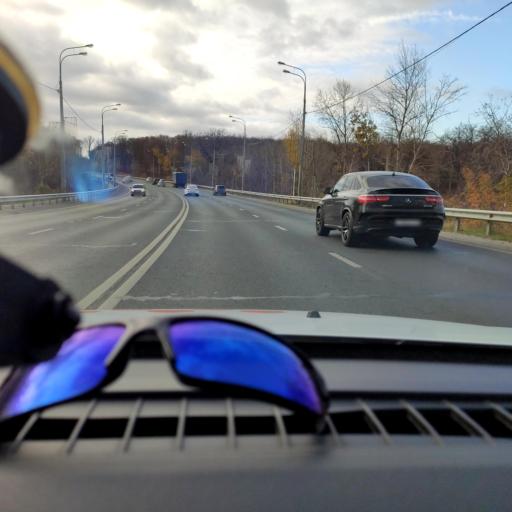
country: RU
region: Samara
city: Samara
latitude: 53.3039
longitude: 50.2267
